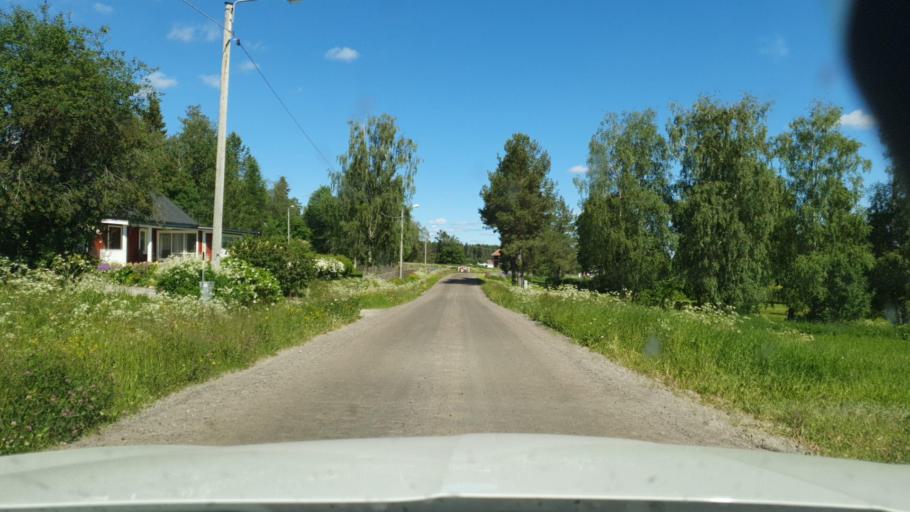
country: SE
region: Vaesterbotten
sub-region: Skelleftea Kommun
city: Byske
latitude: 65.1158
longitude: 21.2039
